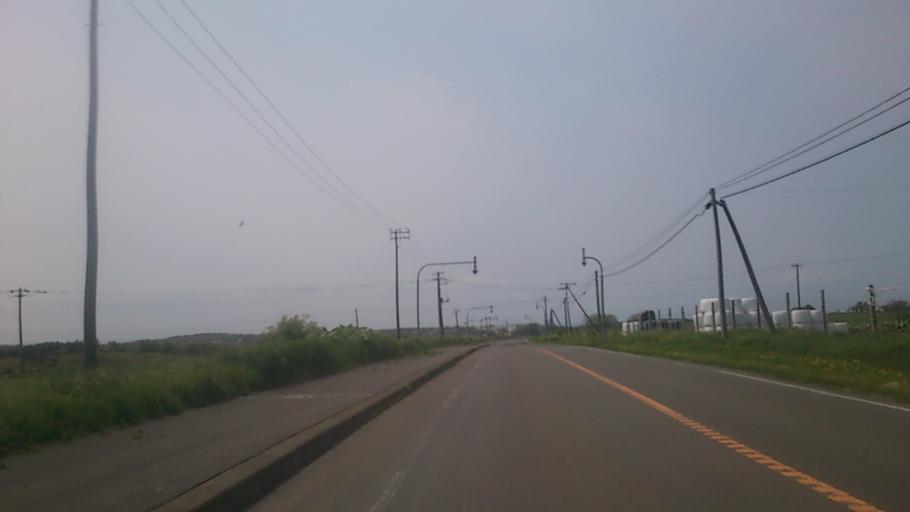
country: JP
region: Hokkaido
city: Nemuro
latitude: 43.2736
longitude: 145.5313
